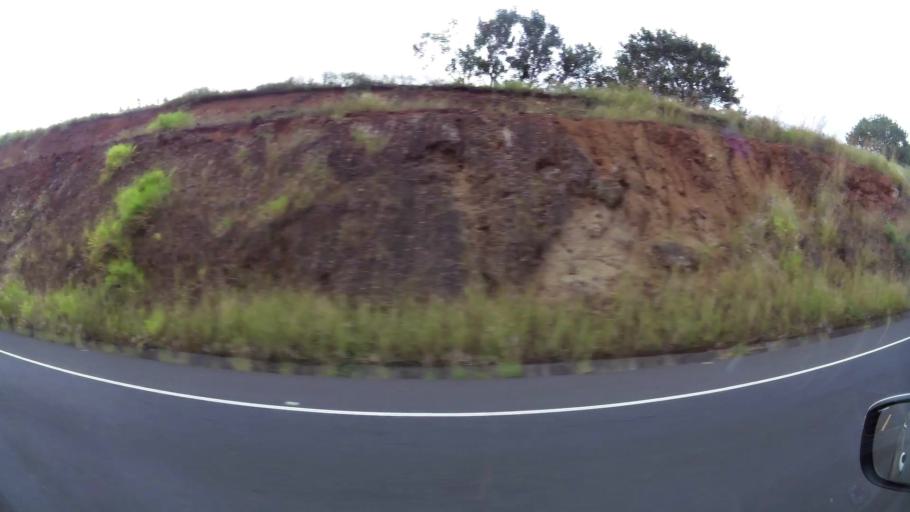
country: CR
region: Alajuela
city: Carrillos
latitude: 9.9660
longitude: -84.3044
